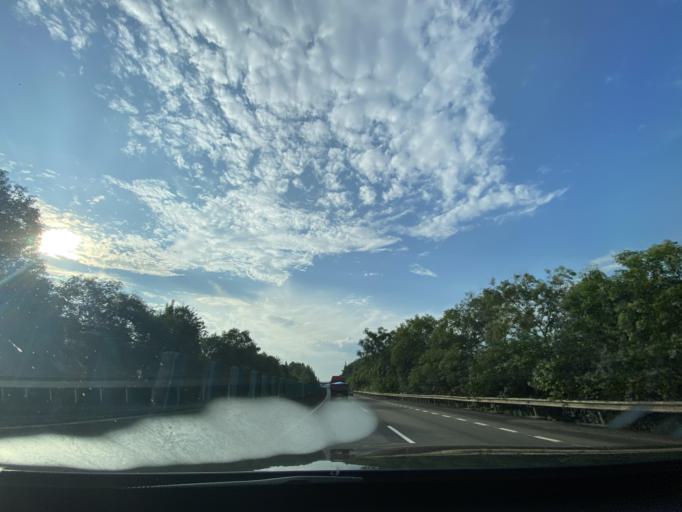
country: CN
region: Sichuan
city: Jiancheng
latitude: 30.3233
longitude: 104.5721
